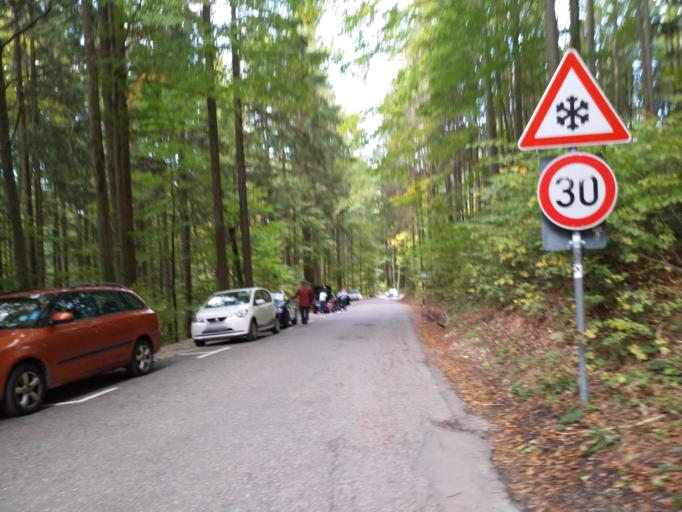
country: AT
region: Tyrol
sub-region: Politischer Bezirk Reutte
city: Vils
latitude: 47.5641
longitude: 10.6401
